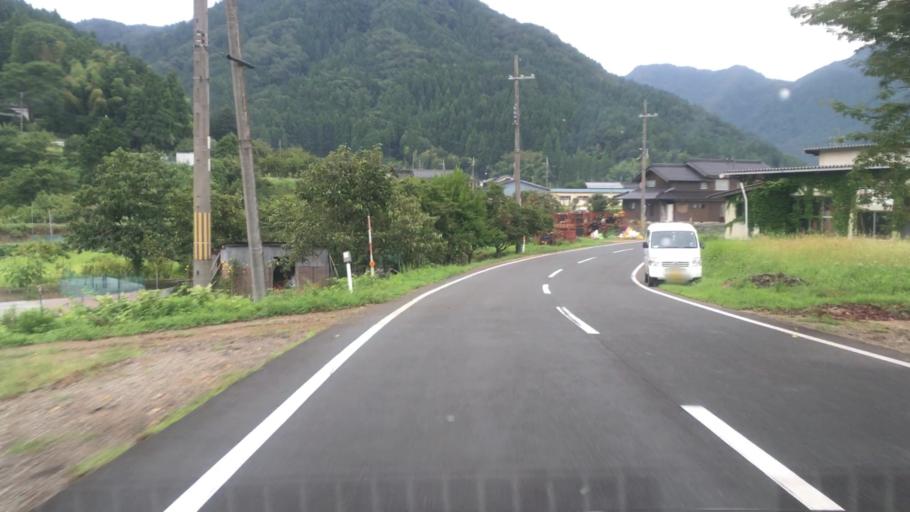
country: JP
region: Hyogo
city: Toyooka
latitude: 35.4559
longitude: 134.7355
